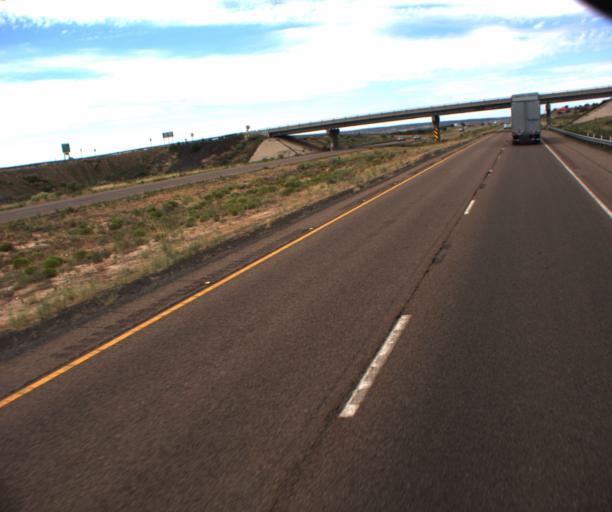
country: US
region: Arizona
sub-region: Apache County
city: Houck
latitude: 35.2392
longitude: -109.3017
